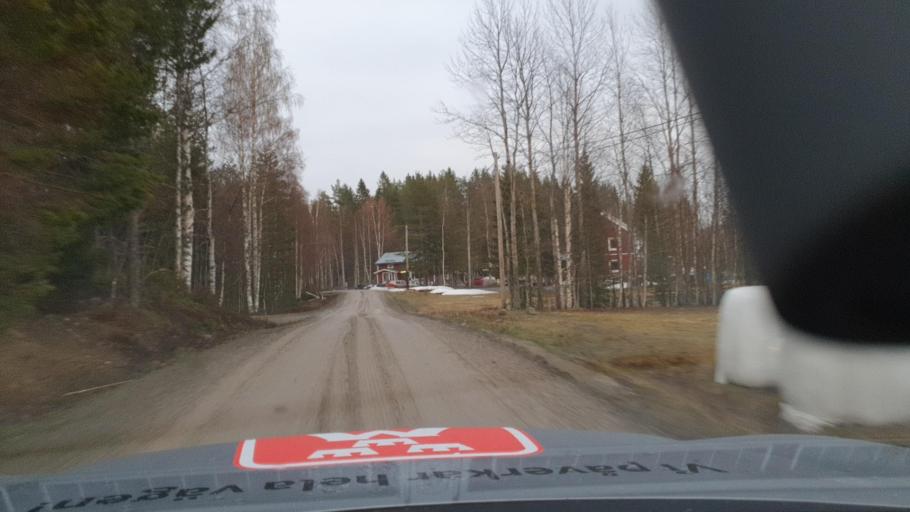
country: SE
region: Vaesternorrland
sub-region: OErnskoeldsviks Kommun
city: Bjasta
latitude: 63.2186
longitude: 18.2853
